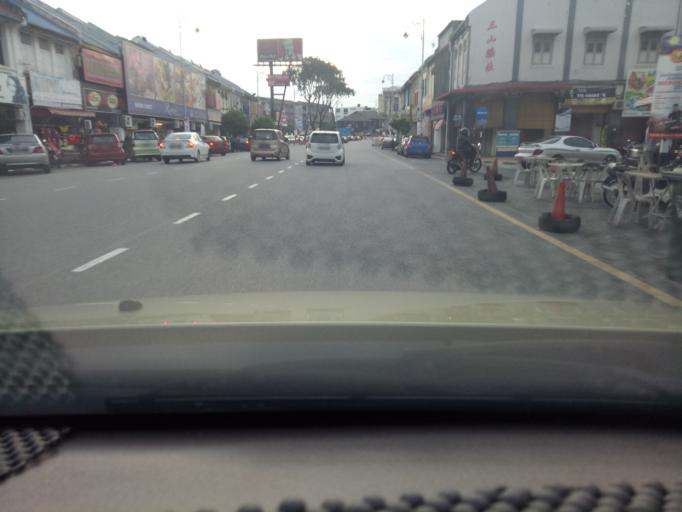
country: MY
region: Kedah
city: Alor Setar
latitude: 6.1166
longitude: 100.3681
